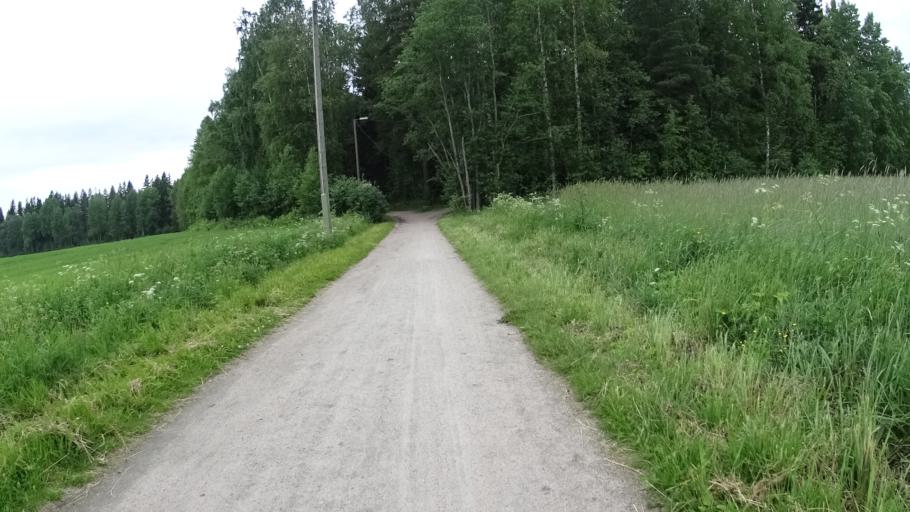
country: FI
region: Uusimaa
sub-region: Helsinki
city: Helsinki
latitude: 60.2640
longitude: 24.9309
